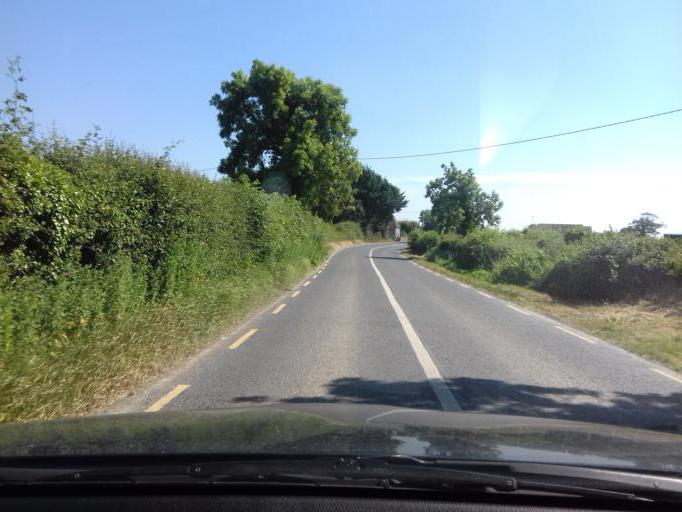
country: IE
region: Leinster
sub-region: Fingal County
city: Swords
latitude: 53.5298
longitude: -6.2692
